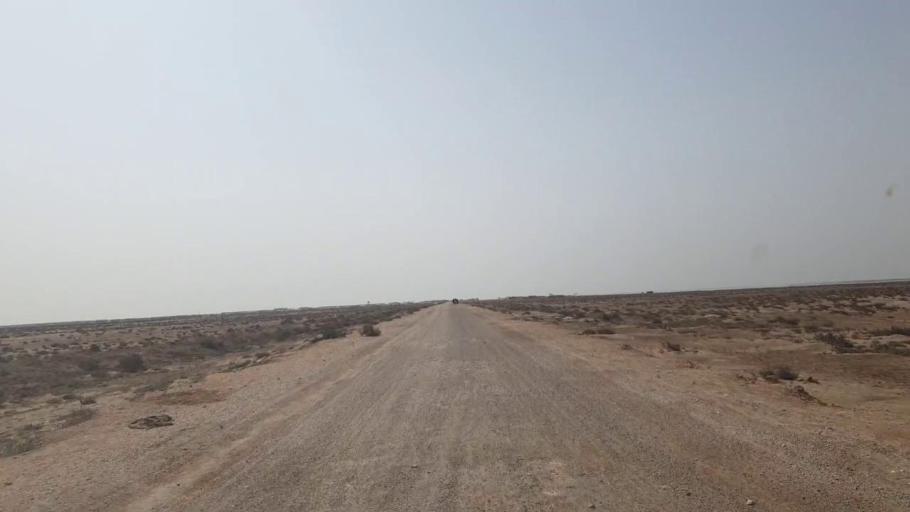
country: PK
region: Sindh
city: Jati
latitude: 24.3505
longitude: 68.5937
